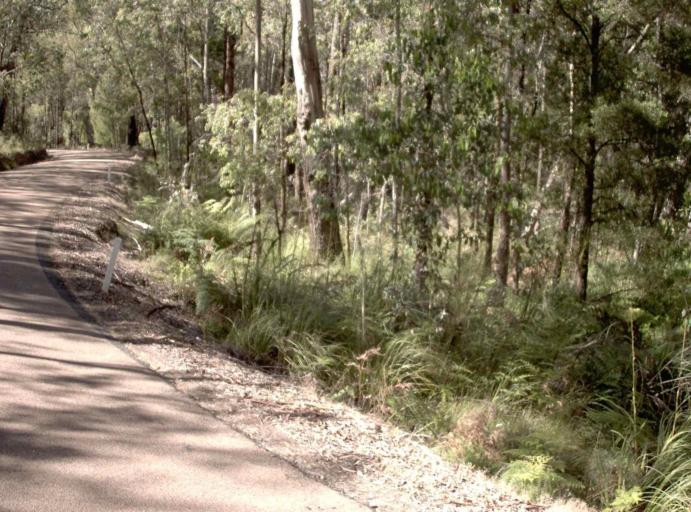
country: AU
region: New South Wales
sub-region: Bombala
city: Bombala
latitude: -37.3772
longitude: 148.6326
